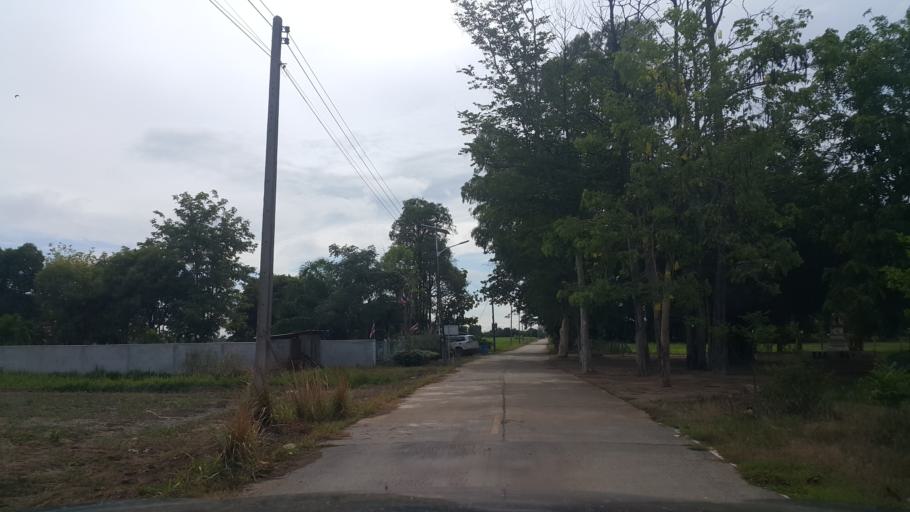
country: TH
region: Sukhothai
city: Sawankhalok
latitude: 17.2656
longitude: 99.9118
